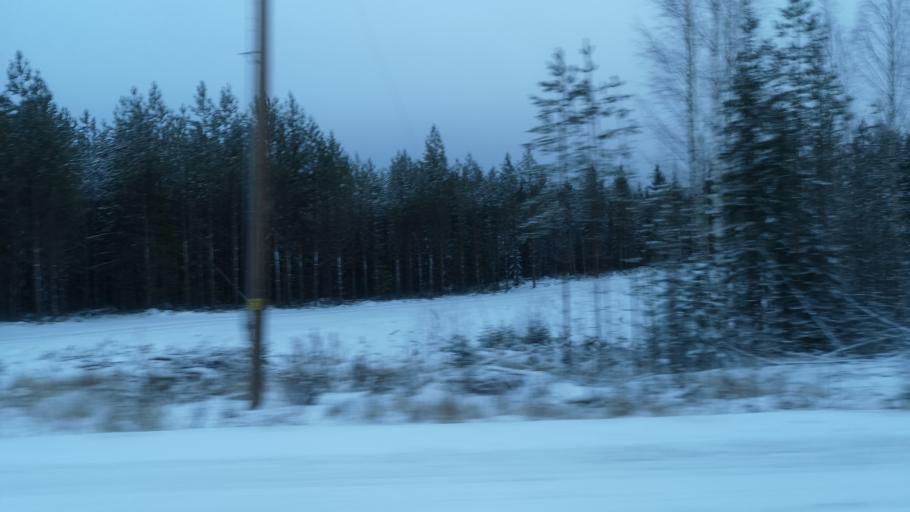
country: FI
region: Southern Savonia
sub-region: Savonlinna
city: Enonkoski
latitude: 62.0513
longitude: 28.7042
